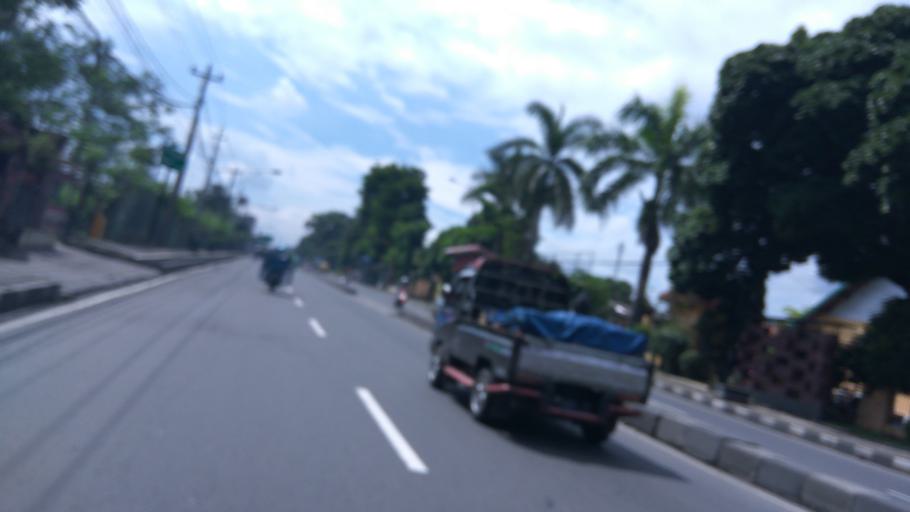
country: ID
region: Central Java
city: Ungaran
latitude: -7.1346
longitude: 110.4042
